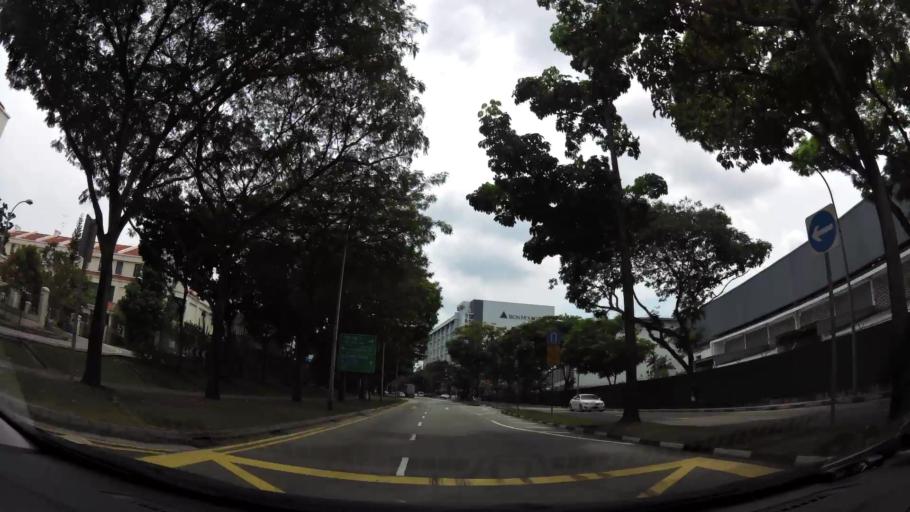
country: MY
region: Johor
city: Johor Bahru
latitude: 1.3388
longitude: 103.7168
